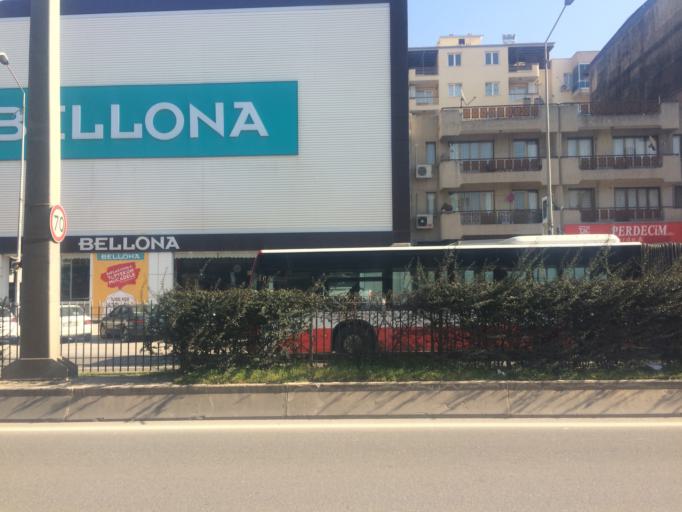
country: TR
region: Izmir
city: Karsiyaka
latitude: 38.4988
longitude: 27.0567
